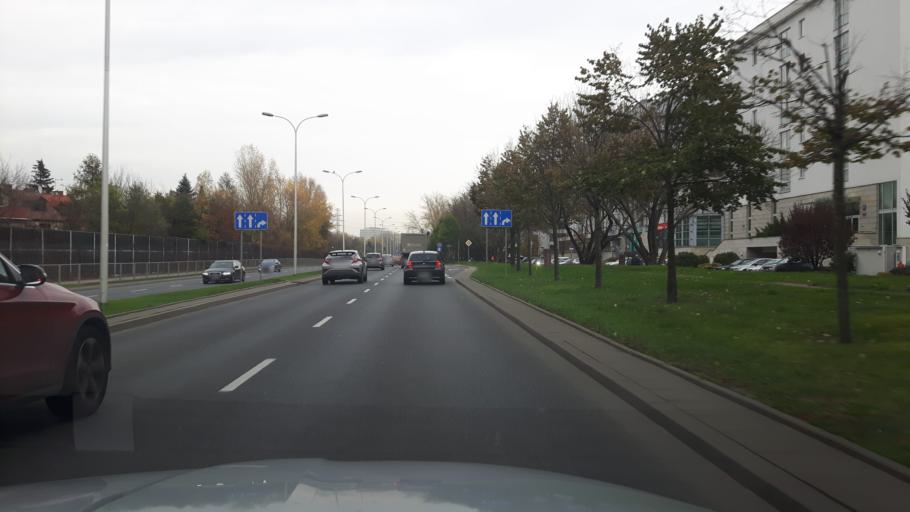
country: PL
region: Masovian Voivodeship
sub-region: Warszawa
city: Ursynow
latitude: 52.1735
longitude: 21.0509
